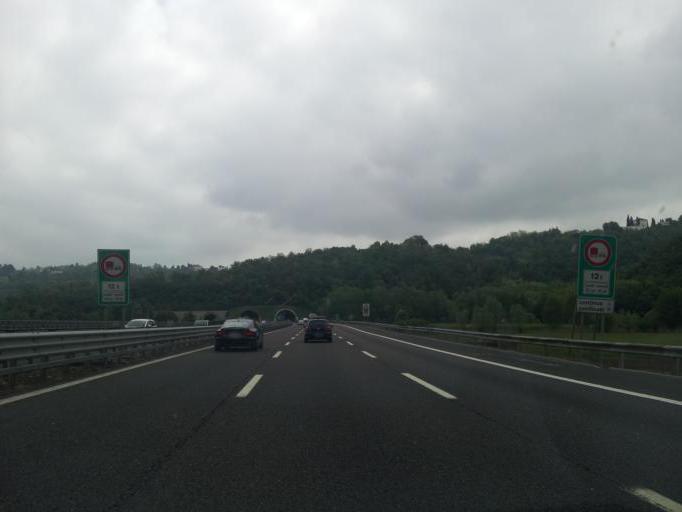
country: IT
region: Veneto
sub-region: Provincia di Vicenza
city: Arcugnano-Torri
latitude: 45.5176
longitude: 11.5278
